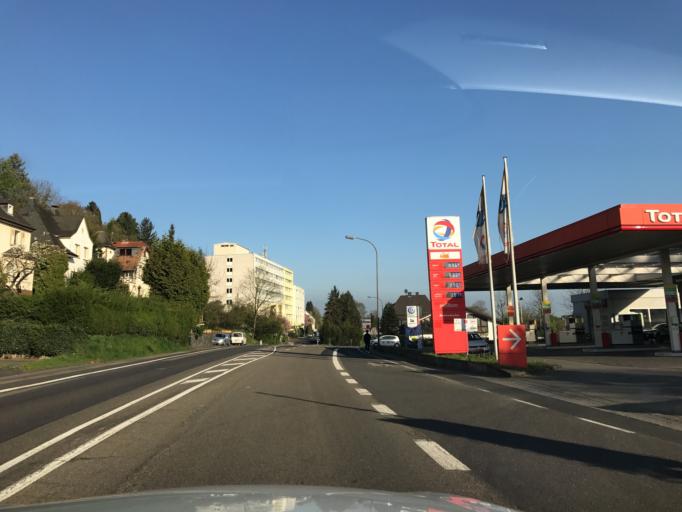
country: DE
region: Rheinland-Pfalz
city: Remagen
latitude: 50.5726
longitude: 7.2355
